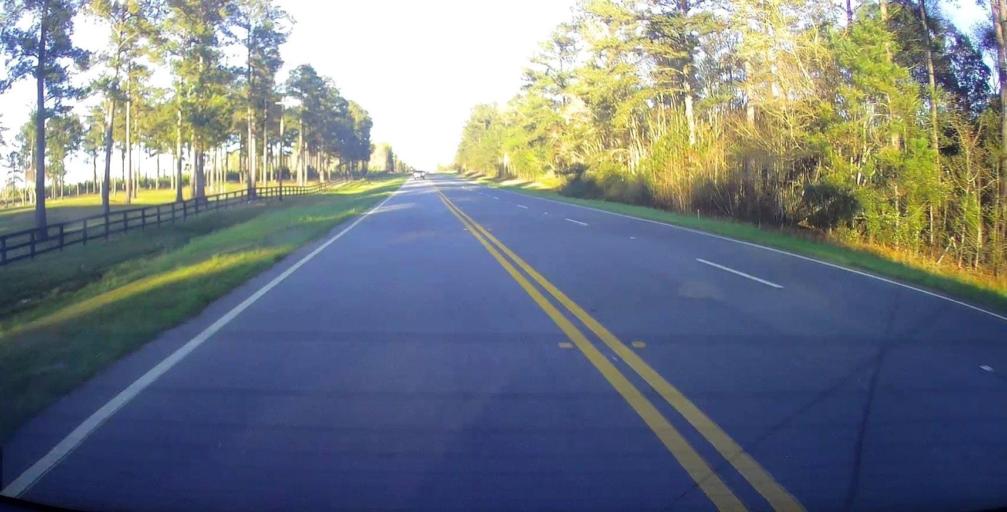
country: US
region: Georgia
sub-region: Wilcox County
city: Abbeville
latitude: 31.9760
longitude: -83.3622
